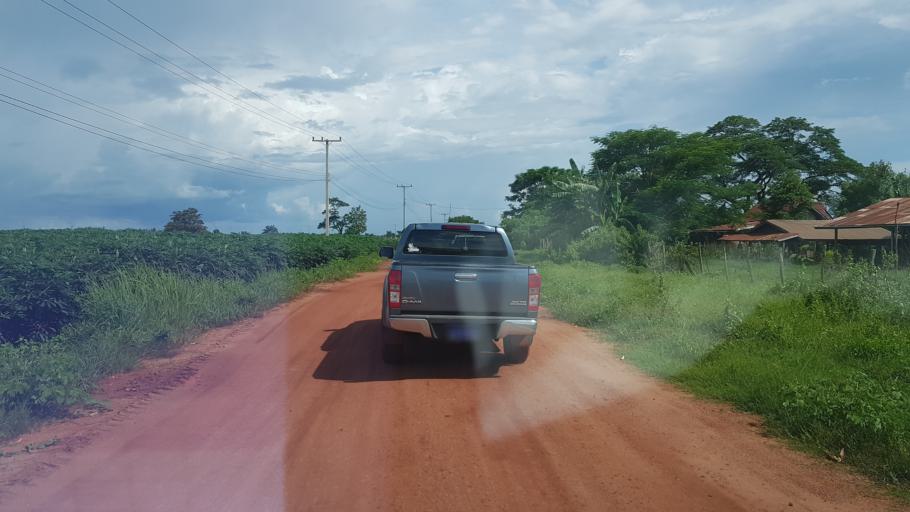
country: LA
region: Vientiane
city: Vientiane
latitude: 18.2223
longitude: 102.5687
